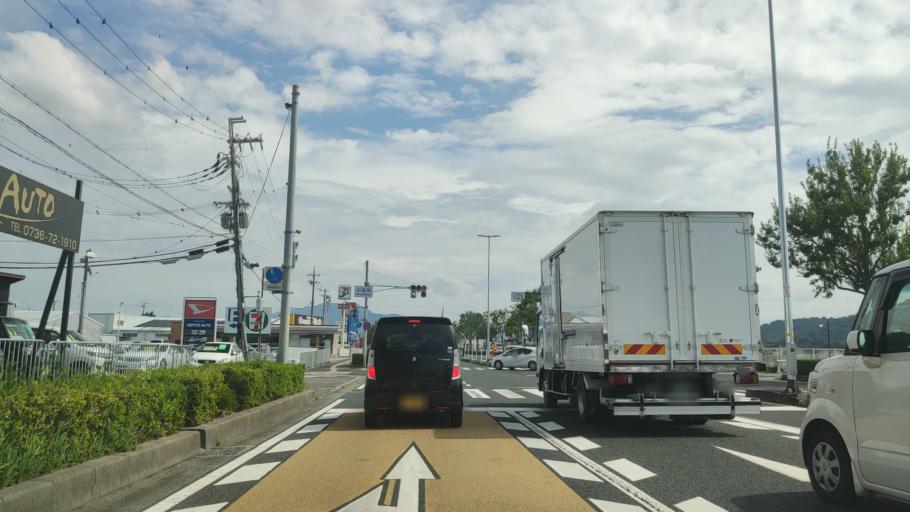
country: JP
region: Wakayama
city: Iwade
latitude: 34.2601
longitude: 135.2987
